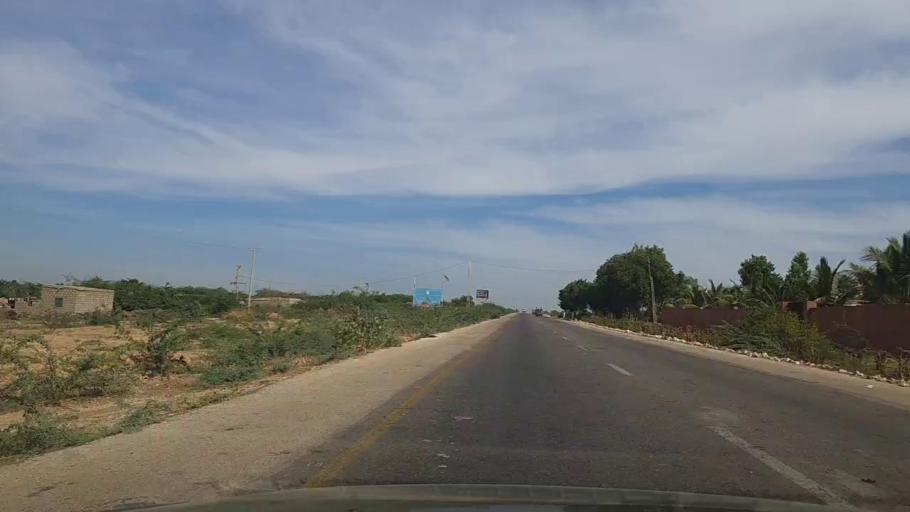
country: PK
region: Sindh
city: Thatta
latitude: 24.8309
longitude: 67.9958
